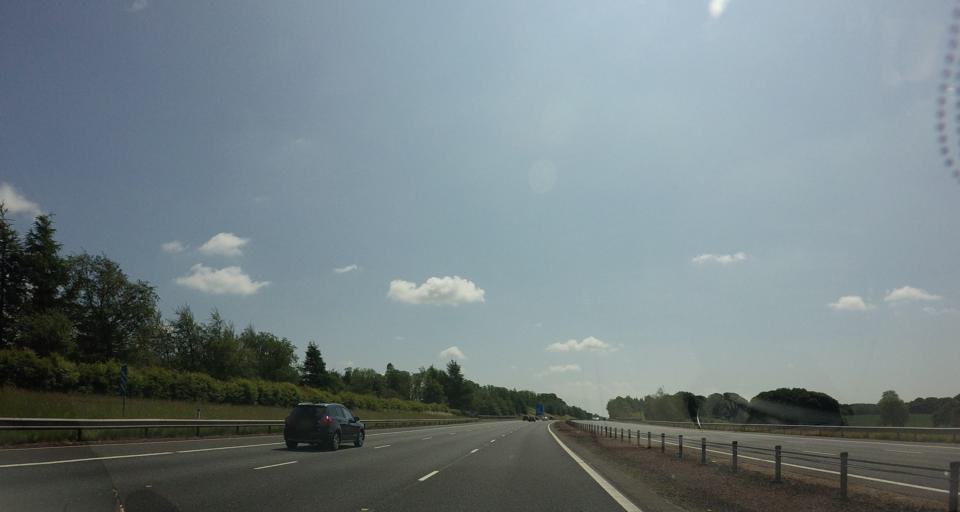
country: GB
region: Scotland
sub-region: Dumfries and Galloway
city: Lockerbie
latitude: 55.1413
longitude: -3.3734
